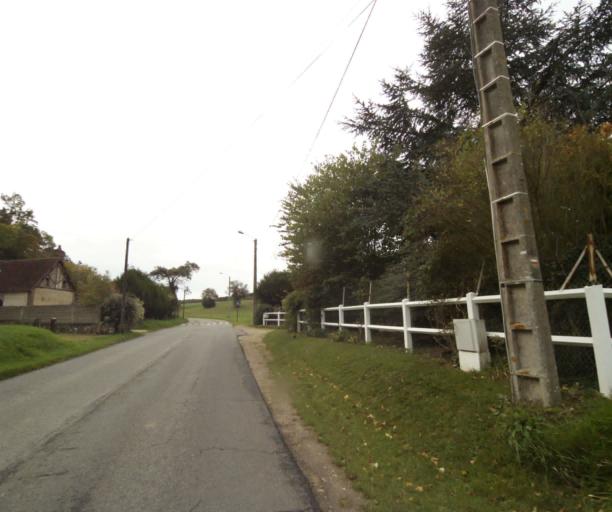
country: FR
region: Centre
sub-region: Departement d'Eure-et-Loir
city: Dreux
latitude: 48.7720
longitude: 1.3496
